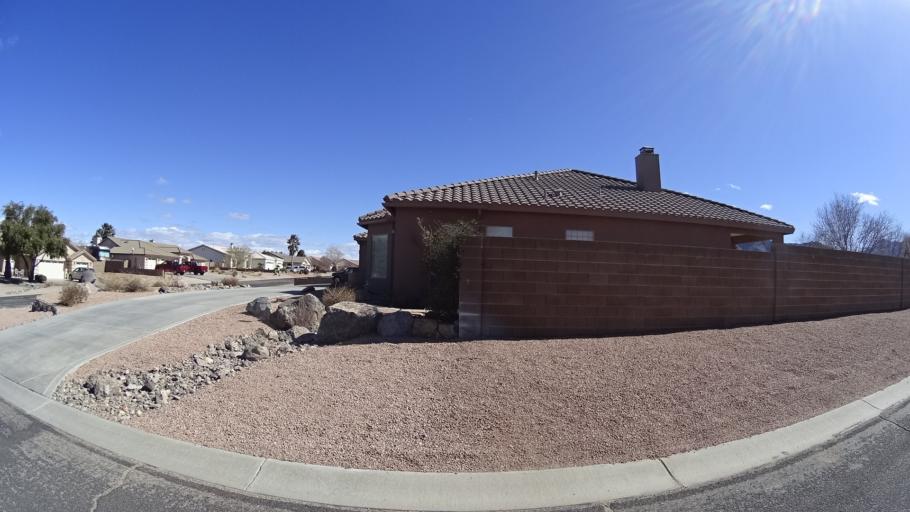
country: US
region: Arizona
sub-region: Mohave County
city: Kingman
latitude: 35.1962
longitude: -113.9754
